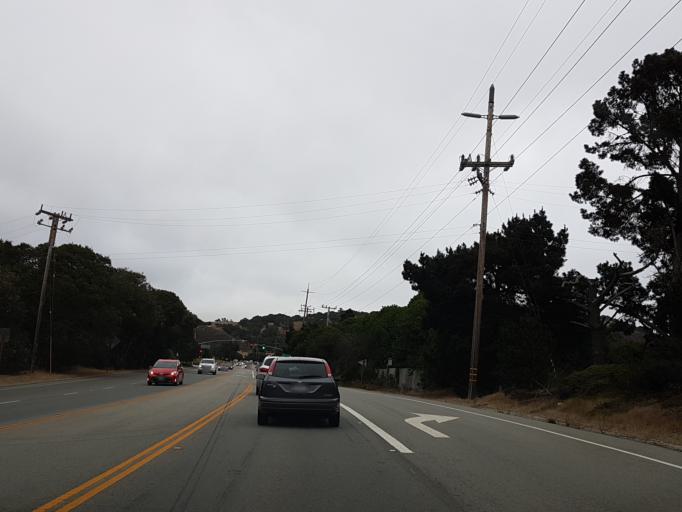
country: US
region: California
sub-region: Monterey County
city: Del Rey Oaks
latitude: 36.5674
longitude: -121.7808
